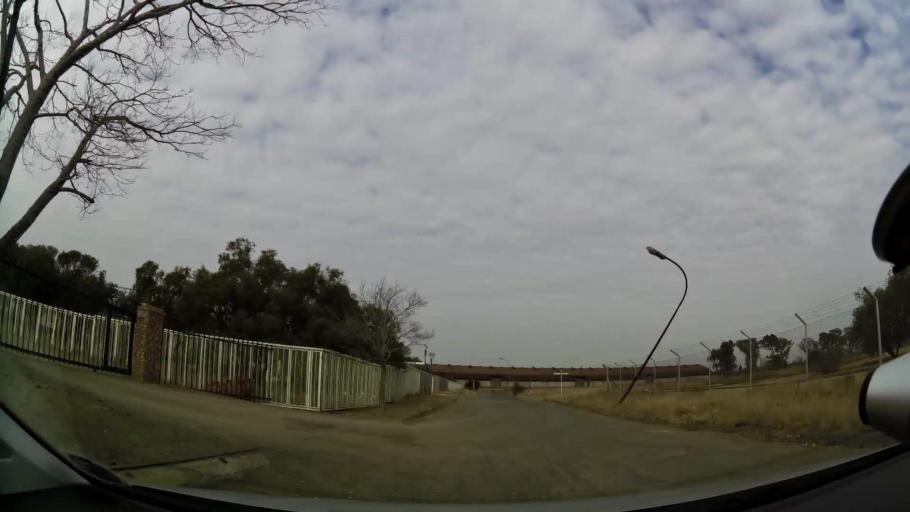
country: ZA
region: Orange Free State
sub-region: Mangaung Metropolitan Municipality
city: Bloemfontein
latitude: -29.1319
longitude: 26.2043
